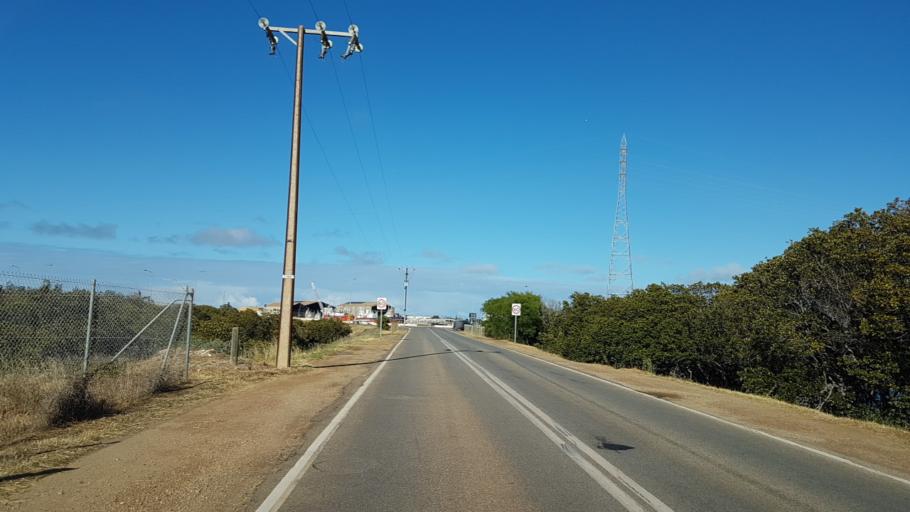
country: AU
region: South Australia
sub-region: Port Adelaide Enfield
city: Birkenhead
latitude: -34.8096
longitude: 138.5267
